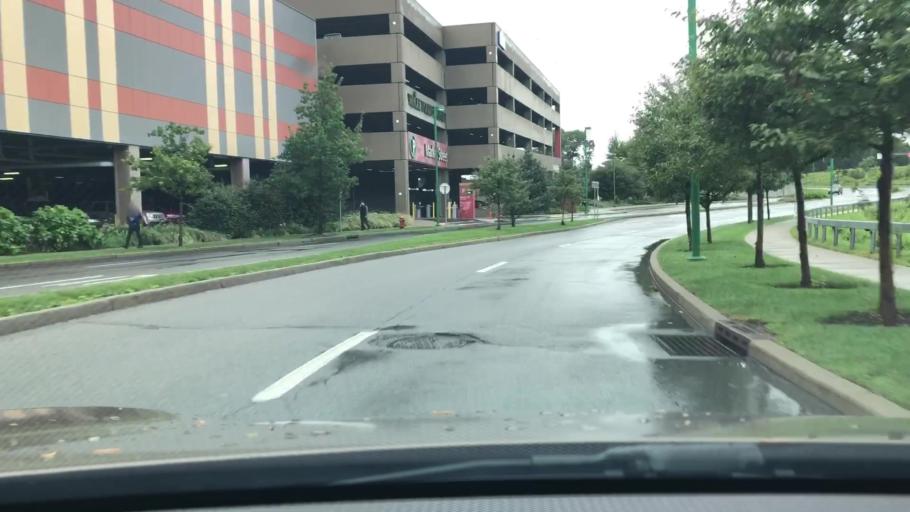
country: US
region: New York
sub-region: Westchester County
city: Tuckahoe
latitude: 40.9618
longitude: -73.8572
